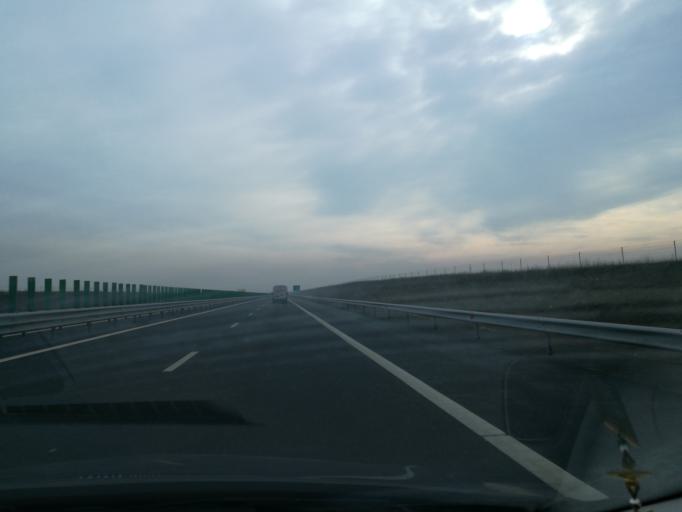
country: RO
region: Constanta
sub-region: Municipiul Medgidia
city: Valea Dacilor
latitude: 44.1953
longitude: 28.2918
